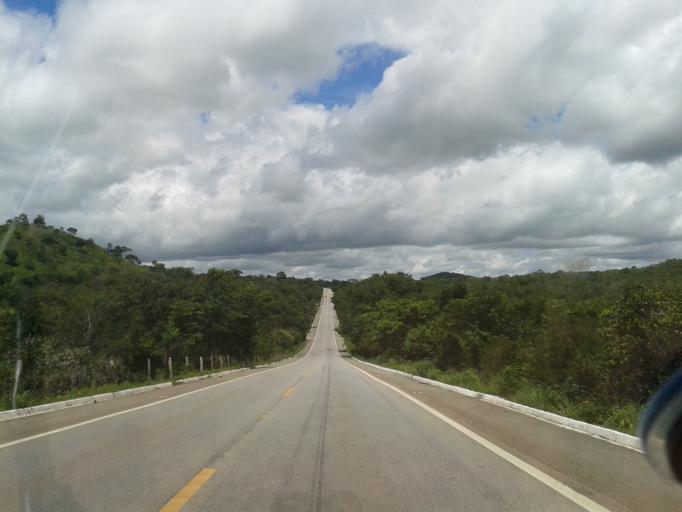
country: BR
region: Goias
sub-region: Goias
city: Goias
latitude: -15.8744
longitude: -50.0946
